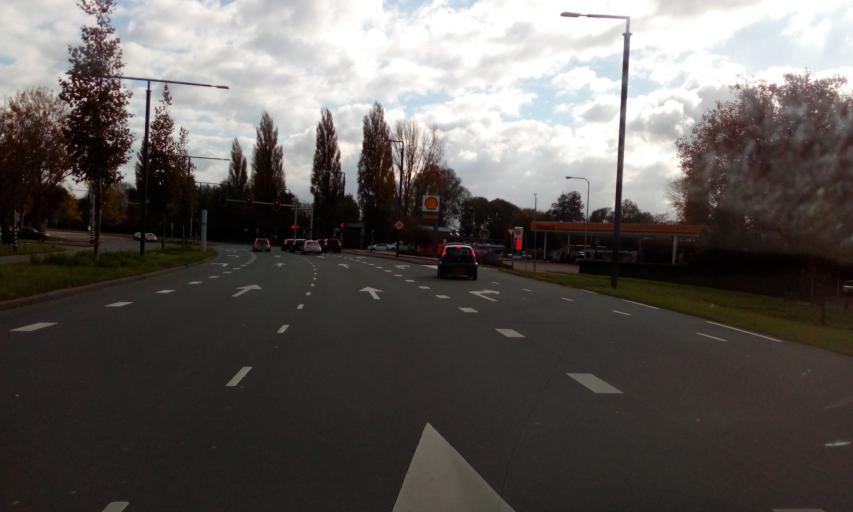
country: NL
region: South Holland
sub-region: Gemeente Dordrecht
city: Dordrecht
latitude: 51.7958
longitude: 4.6558
